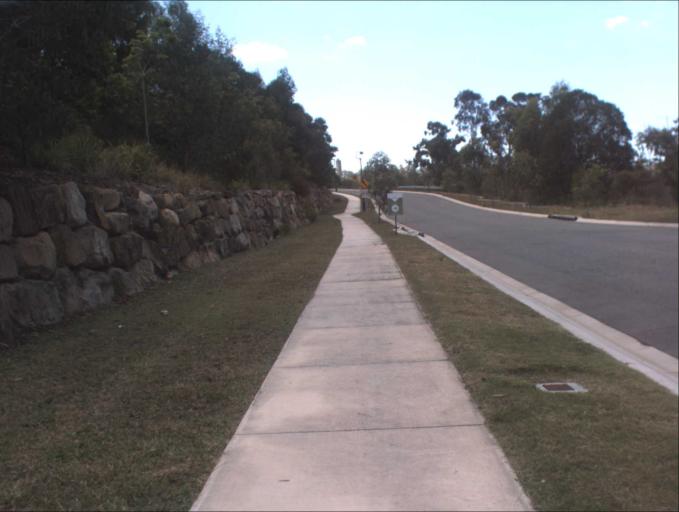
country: AU
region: Queensland
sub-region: Logan
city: Windaroo
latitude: -27.7389
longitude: 153.1859
